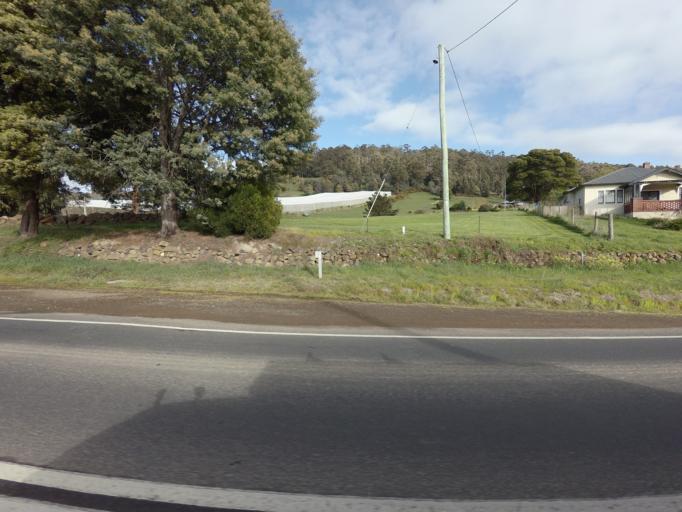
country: AU
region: Tasmania
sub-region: Huon Valley
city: Franklin
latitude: -43.0787
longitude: 147.0173
